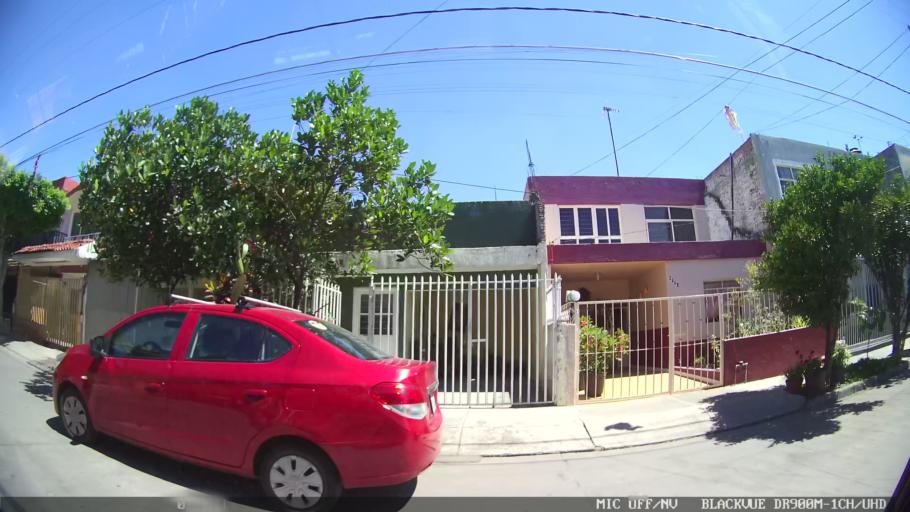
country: MX
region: Jalisco
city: Tlaquepaque
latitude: 20.6630
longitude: -103.2834
